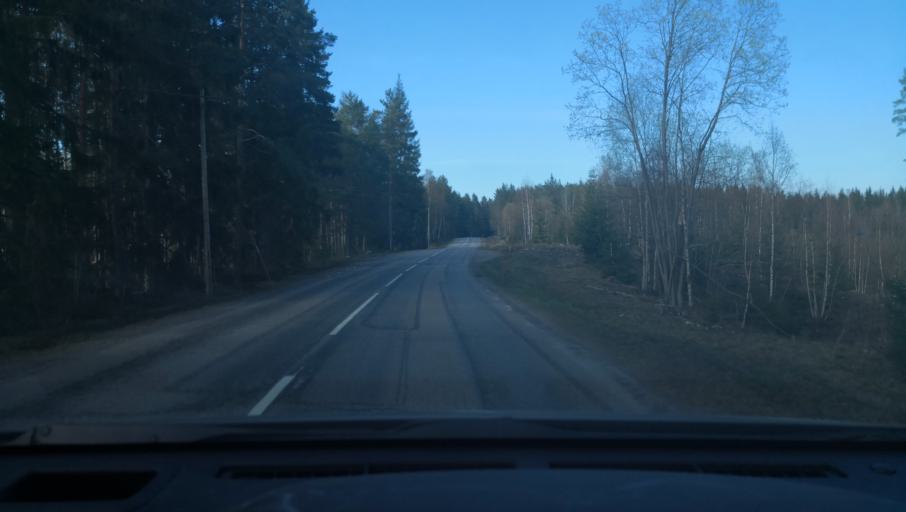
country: SE
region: Uppsala
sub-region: Heby Kommun
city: Morgongava
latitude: 59.9961
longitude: 16.9259
